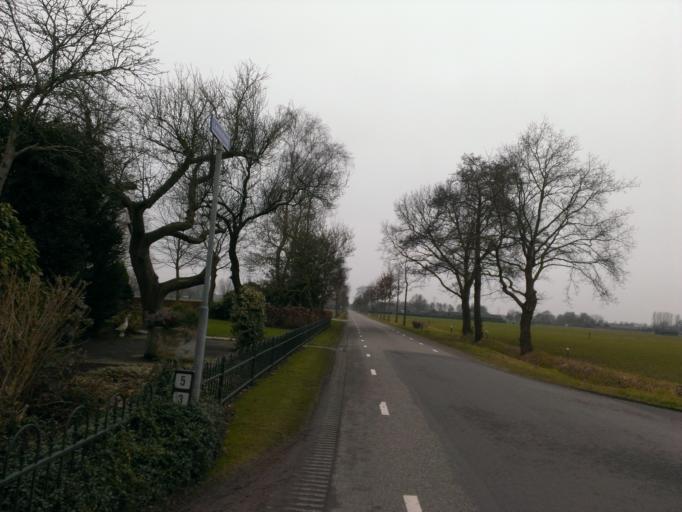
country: NL
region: Gelderland
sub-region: Gemeente Voorst
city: Twello
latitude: 52.2211
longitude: 6.0671
